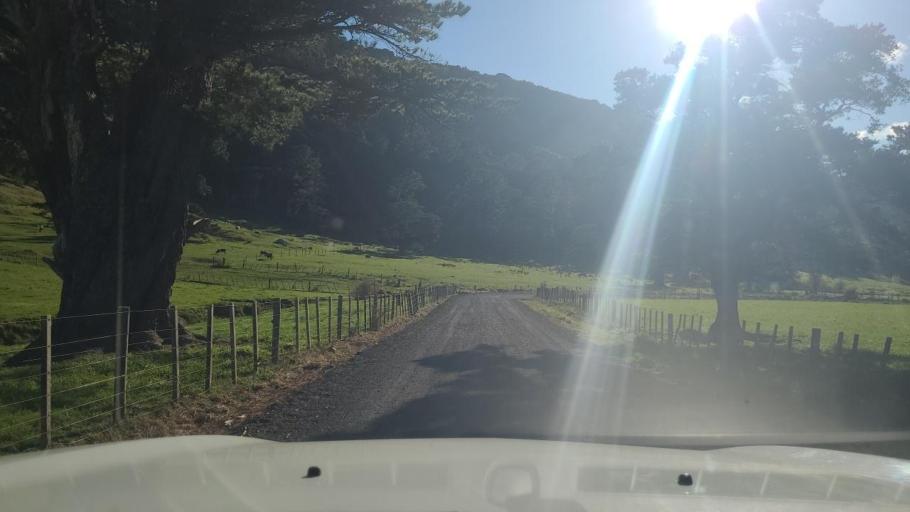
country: NZ
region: Bay of Plenty
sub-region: Western Bay of Plenty District
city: Katikati
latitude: -37.5620
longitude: 175.7448
